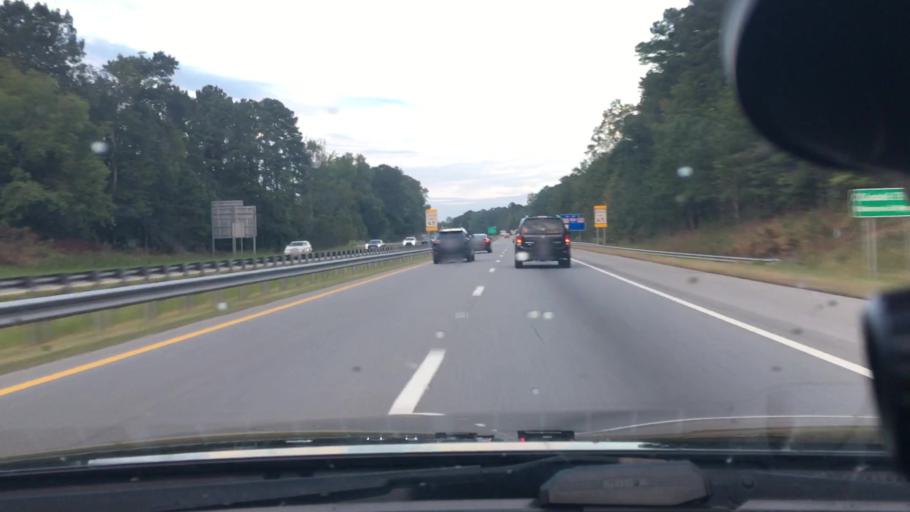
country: US
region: North Carolina
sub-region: Wake County
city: Apex
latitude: 35.7081
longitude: -78.8493
